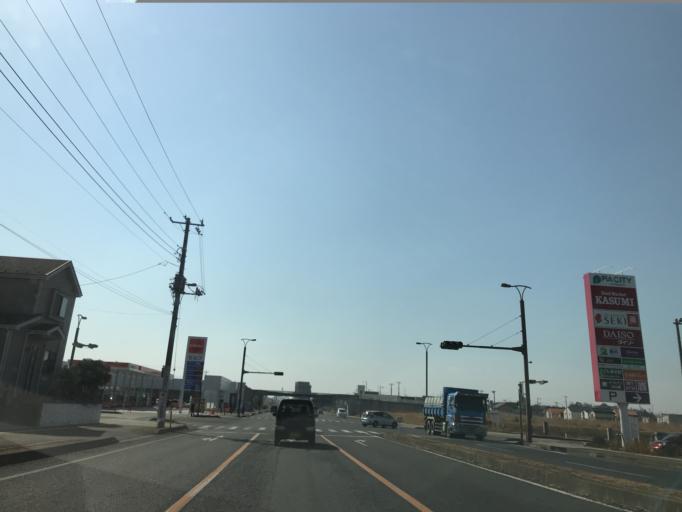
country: JP
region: Ibaraki
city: Mitsukaido
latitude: 36.0041
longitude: 140.0340
